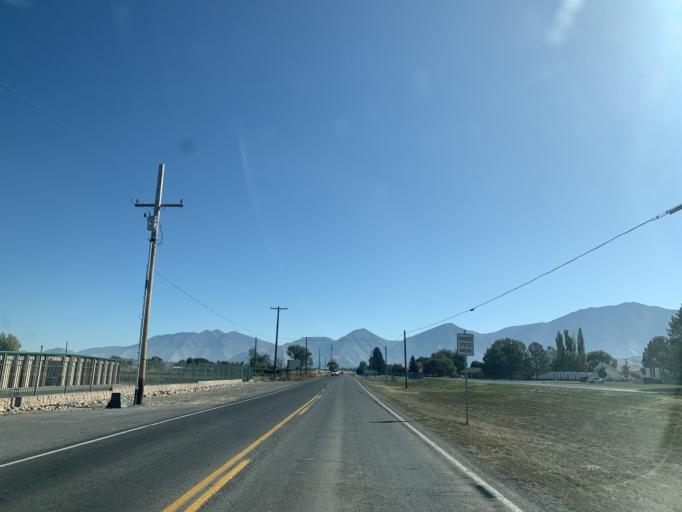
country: US
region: Utah
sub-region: Utah County
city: West Mountain
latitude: 40.0411
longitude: -111.7681
